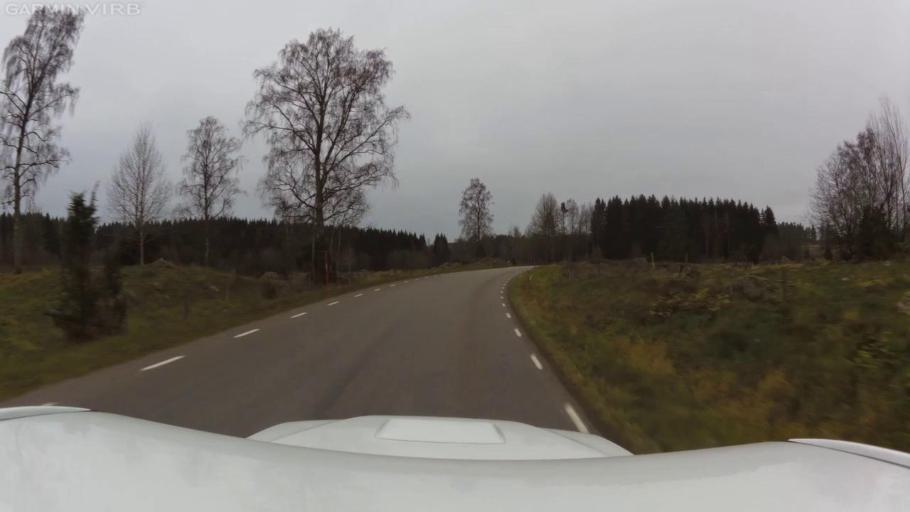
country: SE
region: OEstergoetland
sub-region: Linkopings Kommun
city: Vikingstad
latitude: 58.2303
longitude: 15.3959
